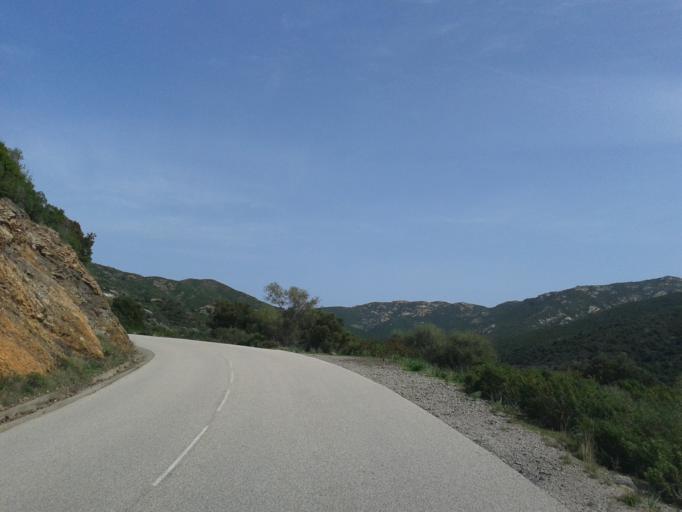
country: FR
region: Corsica
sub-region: Departement de la Haute-Corse
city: Monticello
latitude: 42.6524
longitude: 9.1129
